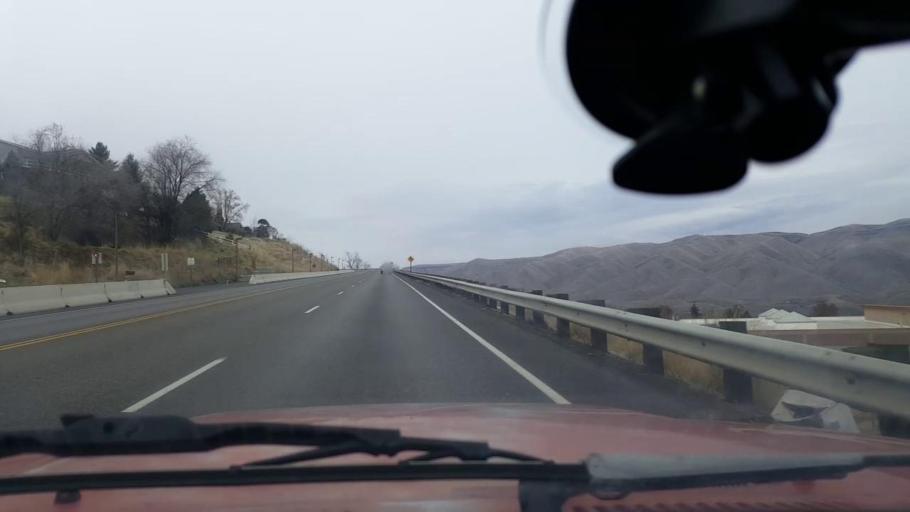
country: US
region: Washington
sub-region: Asotin County
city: West Clarkston-Highland
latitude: 46.3995
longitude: -117.0718
